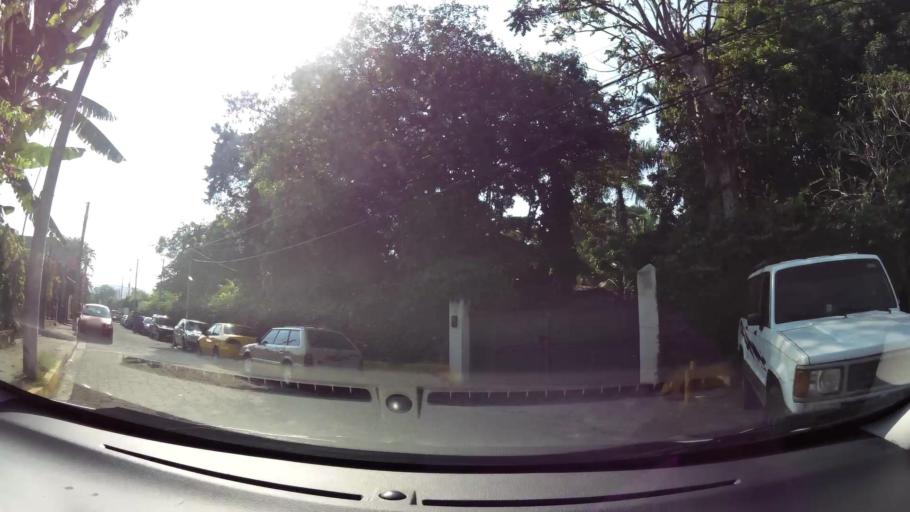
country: SV
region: La Libertad
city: Antiguo Cuscatlan
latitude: 13.6721
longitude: -89.2419
